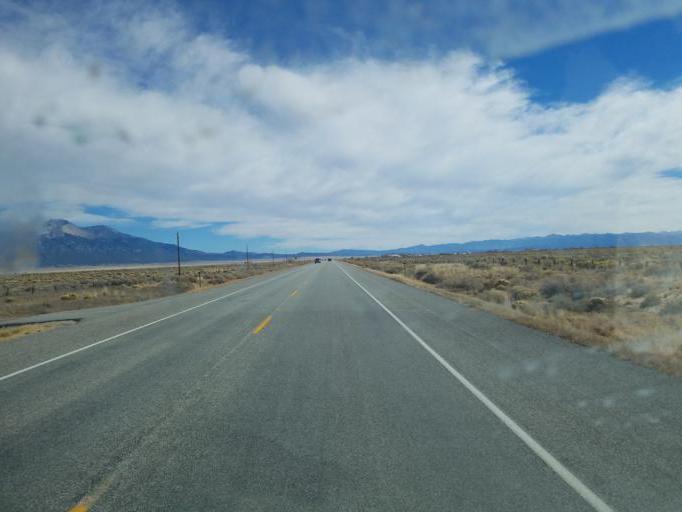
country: US
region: Colorado
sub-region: Alamosa County
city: Alamosa East
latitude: 37.4745
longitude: -105.7206
